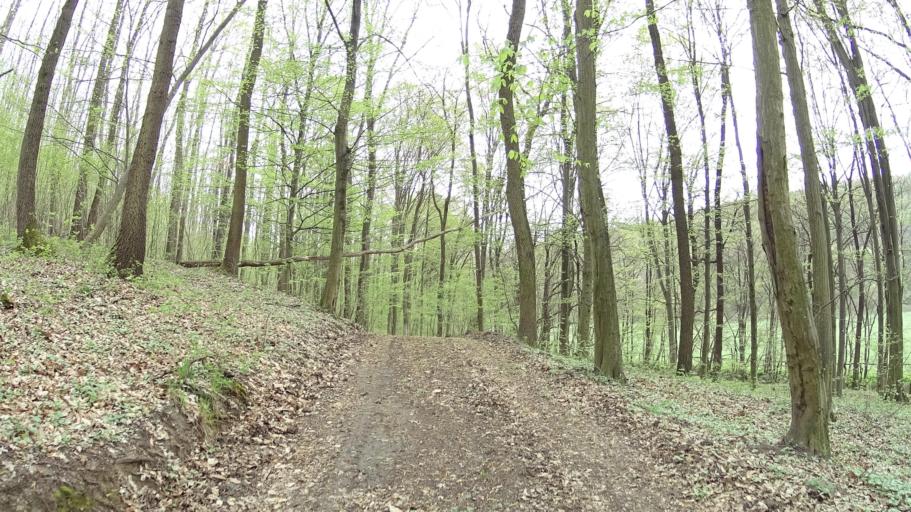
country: HU
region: Pest
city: Veroce
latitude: 47.8797
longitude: 19.0704
